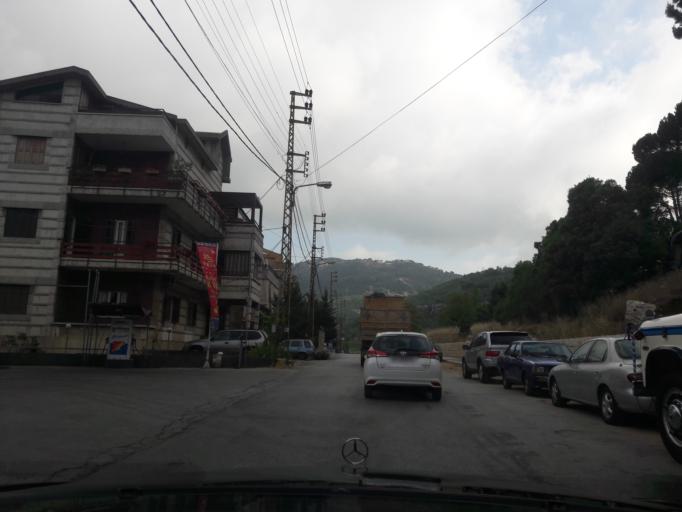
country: LB
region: Mont-Liban
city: Djounie
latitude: 33.9245
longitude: 35.7302
